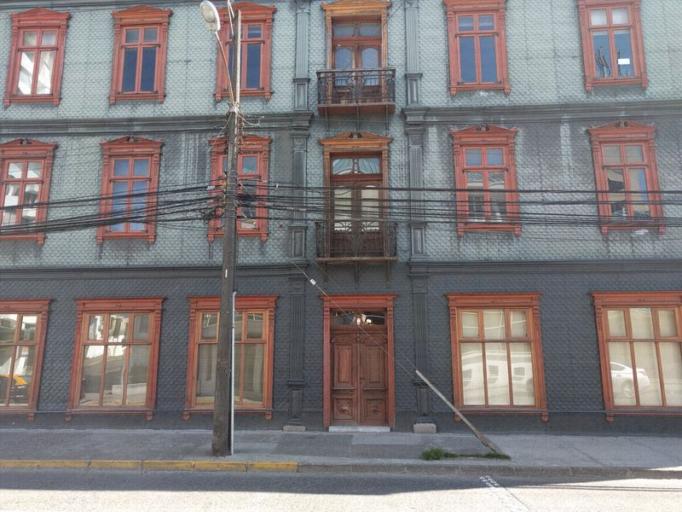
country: CL
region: Los Rios
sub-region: Provincia de Valdivia
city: Valdivia
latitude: -39.8142
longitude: -73.2479
